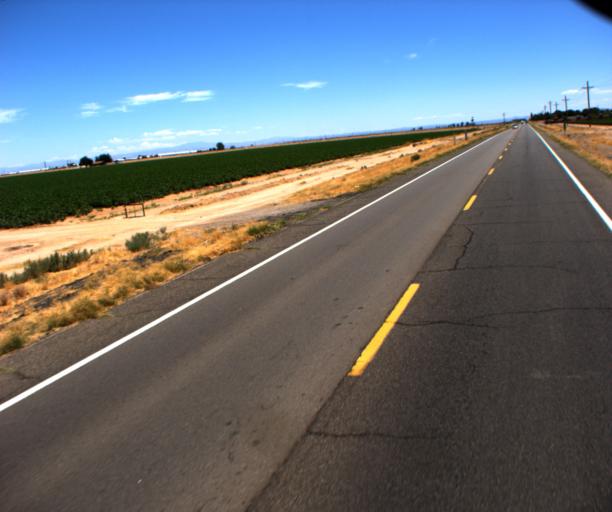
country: US
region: Arizona
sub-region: Pinal County
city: Casa Grande
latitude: 32.8797
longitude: -111.6674
